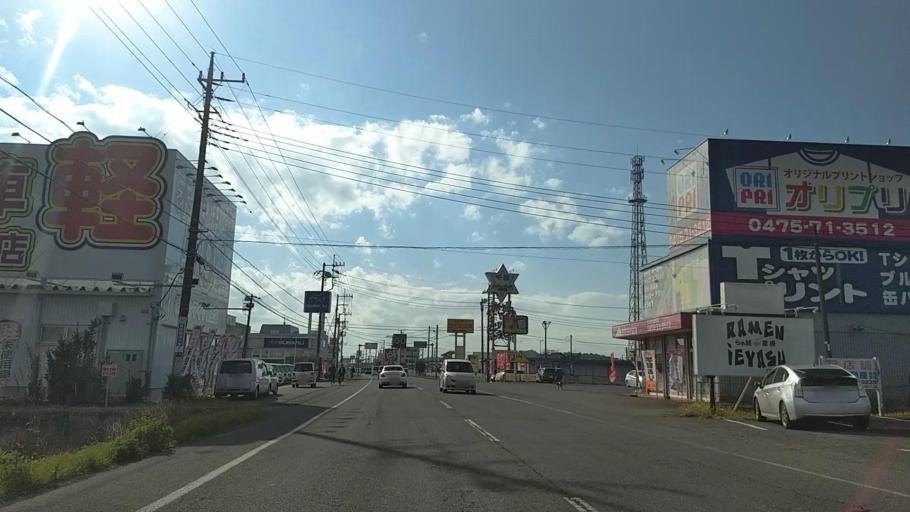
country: JP
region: Chiba
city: Naruto
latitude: 35.5886
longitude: 140.3919
